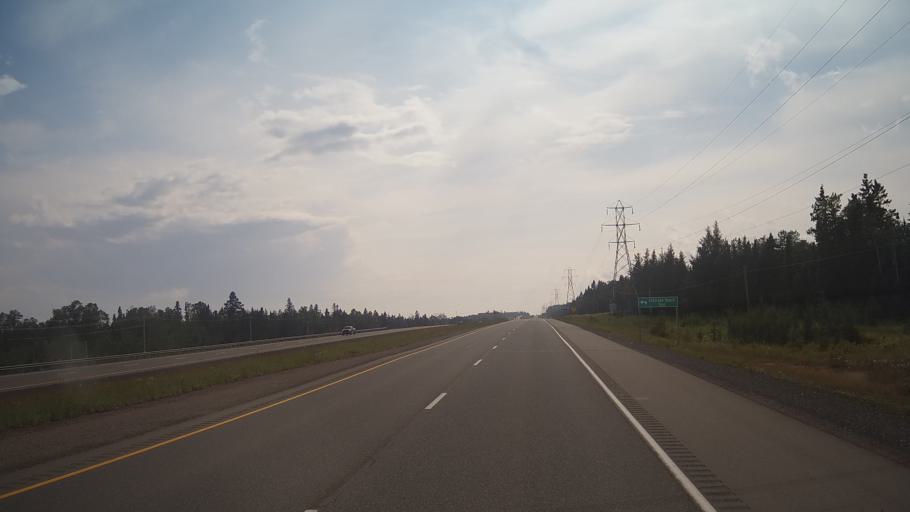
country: CA
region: Ontario
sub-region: Thunder Bay District
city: Thunder Bay
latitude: 48.5804
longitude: -88.8067
